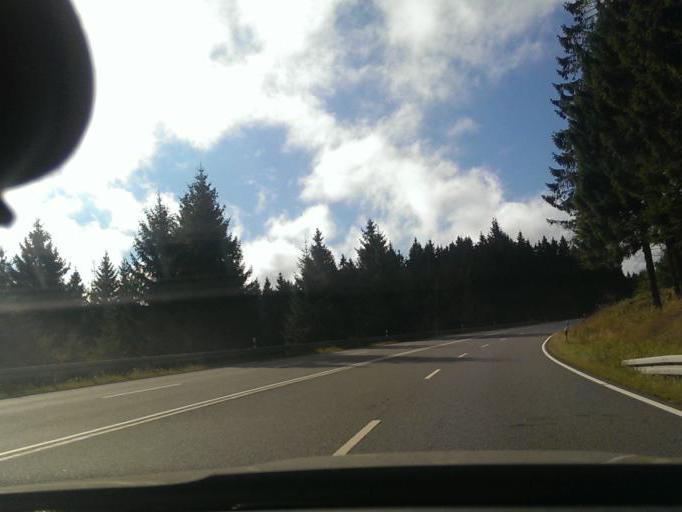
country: DE
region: Lower Saxony
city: Bad Harzburg
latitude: 51.8183
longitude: 10.5246
